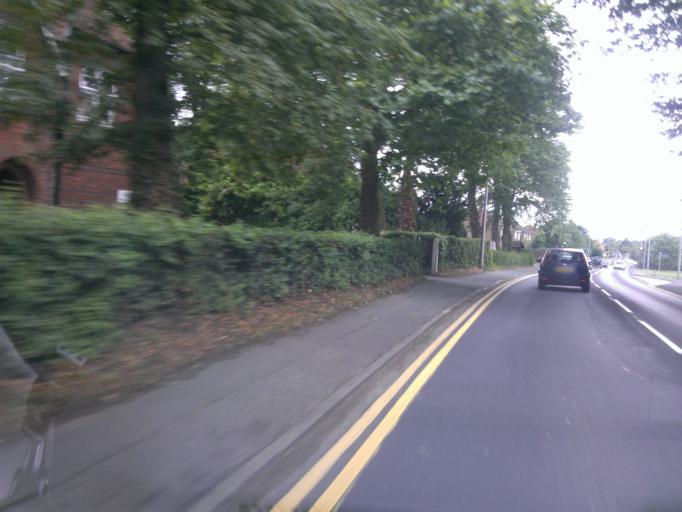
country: GB
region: England
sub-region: Essex
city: Colchester
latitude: 51.9119
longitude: 0.9283
